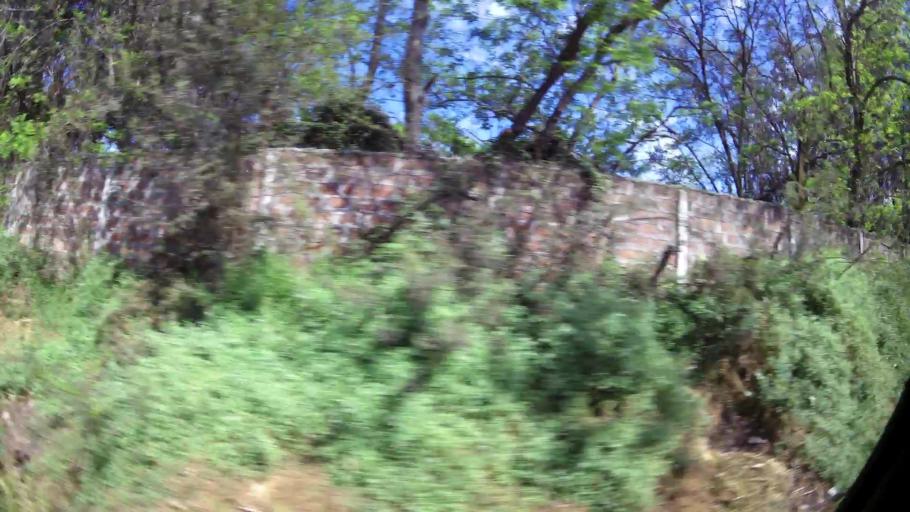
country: CL
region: Santiago Metropolitan
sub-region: Provincia de Talagante
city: Talagante
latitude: -33.6776
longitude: -70.9524
